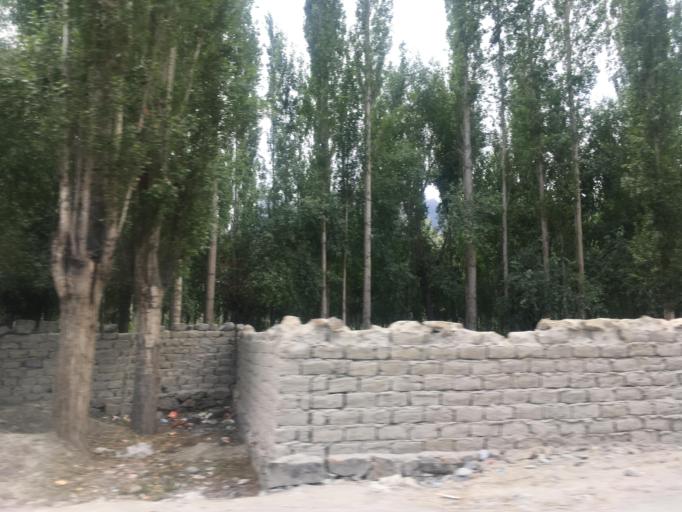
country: PK
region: Gilgit-Baltistan
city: Skardu
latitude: 35.2925
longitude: 75.6133
